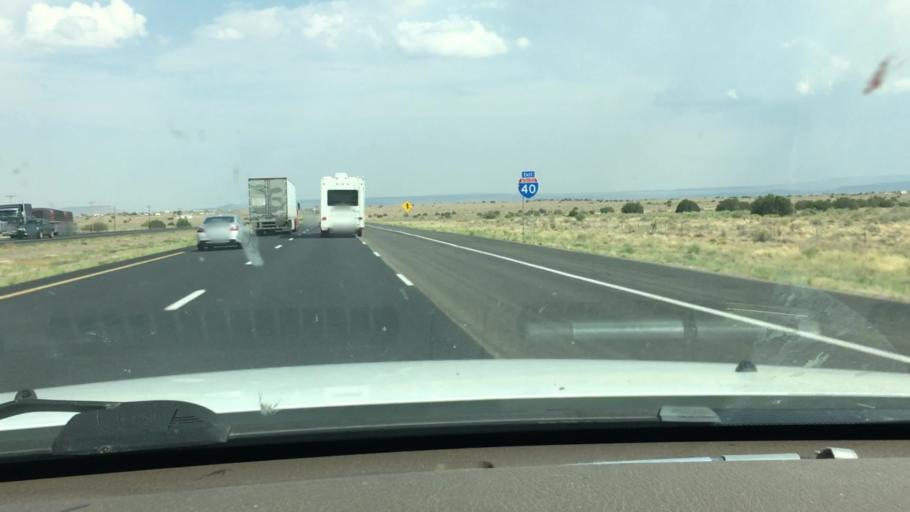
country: US
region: New Mexico
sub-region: Cibola County
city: Laguna
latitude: 35.0090
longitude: -107.3188
